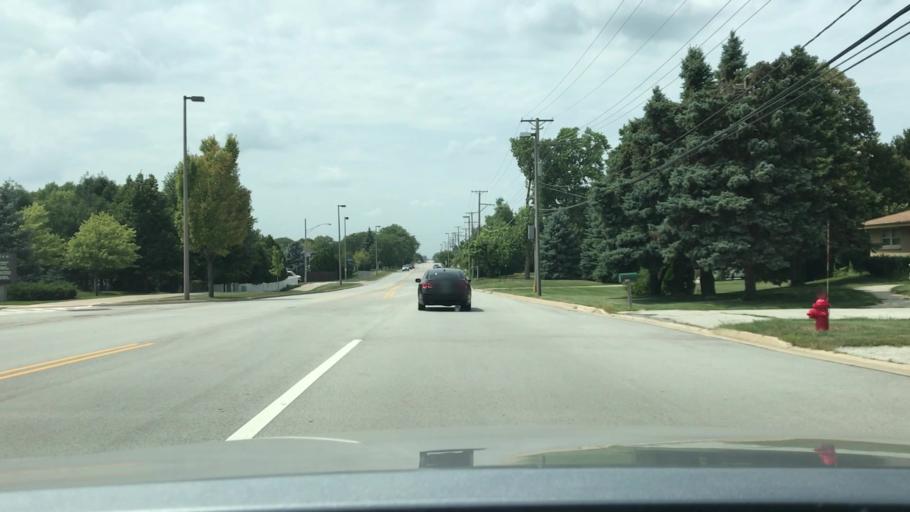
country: US
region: Illinois
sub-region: DuPage County
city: Woodridge
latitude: 41.7366
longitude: -88.0144
